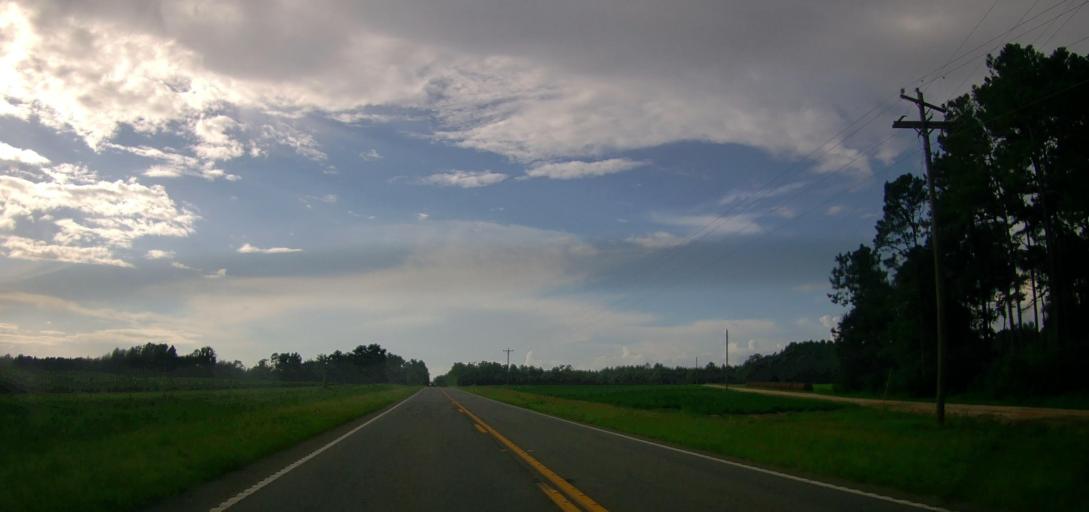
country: US
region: Georgia
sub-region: Ware County
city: Deenwood
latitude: 31.3165
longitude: -82.5721
